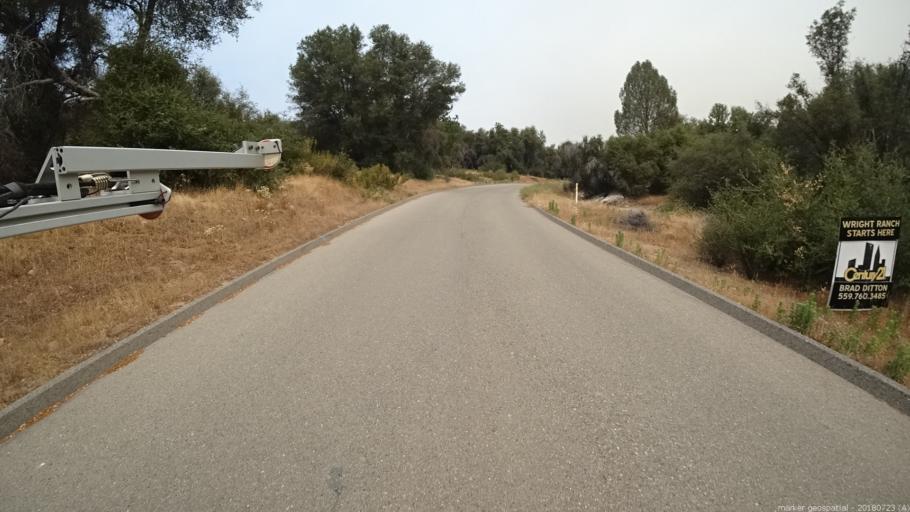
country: US
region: California
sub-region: Madera County
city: Oakhurst
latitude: 37.3443
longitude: -119.6680
